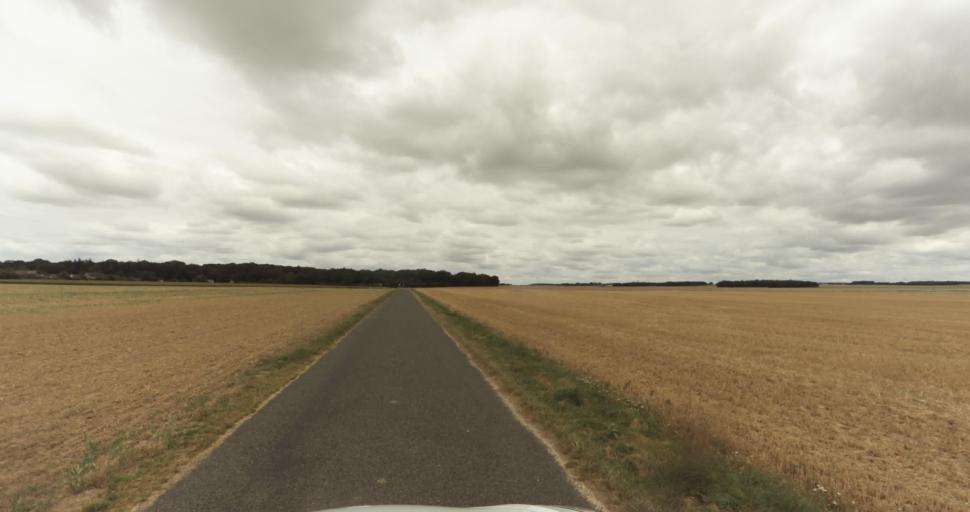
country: FR
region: Haute-Normandie
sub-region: Departement de l'Eure
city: Nonancourt
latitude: 48.8007
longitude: 1.1228
